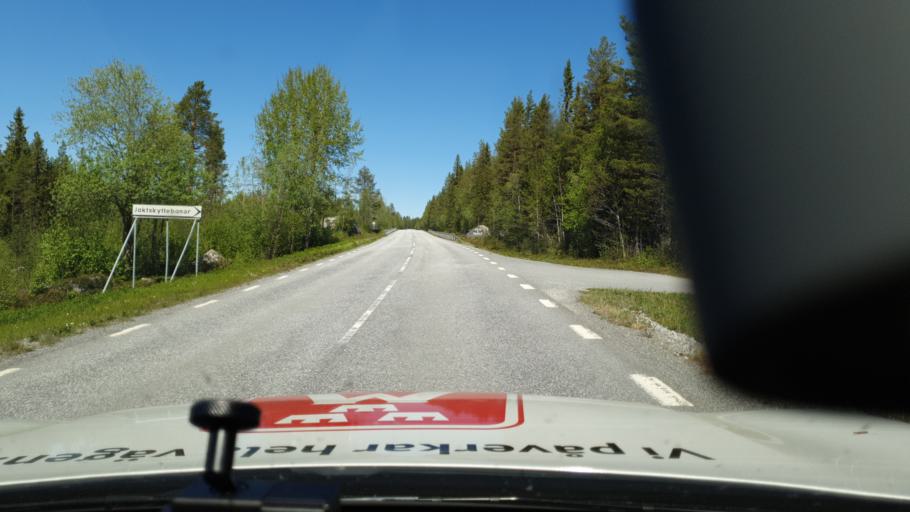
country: SE
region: Vaesterbotten
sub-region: Storumans Kommun
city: Storuman
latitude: 65.1299
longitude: 17.1081
